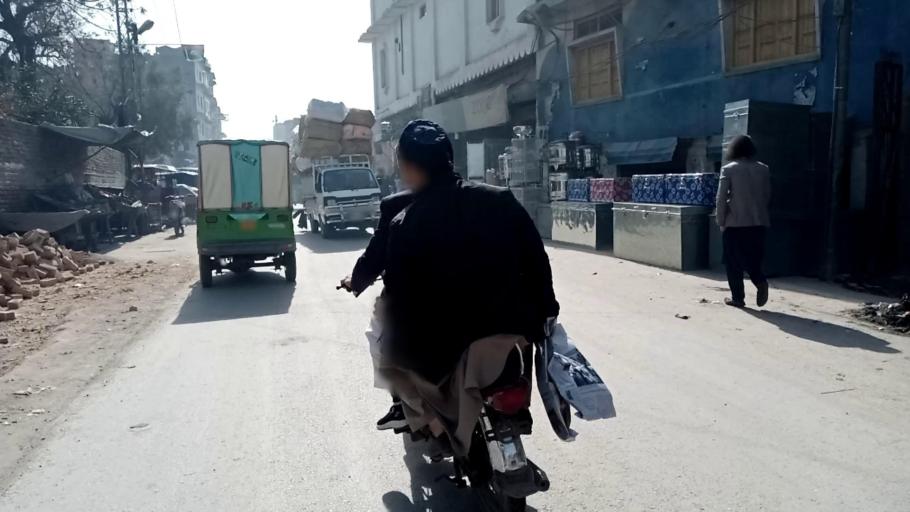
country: PK
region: Khyber Pakhtunkhwa
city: Peshawar
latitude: 34.0026
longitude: 71.5855
